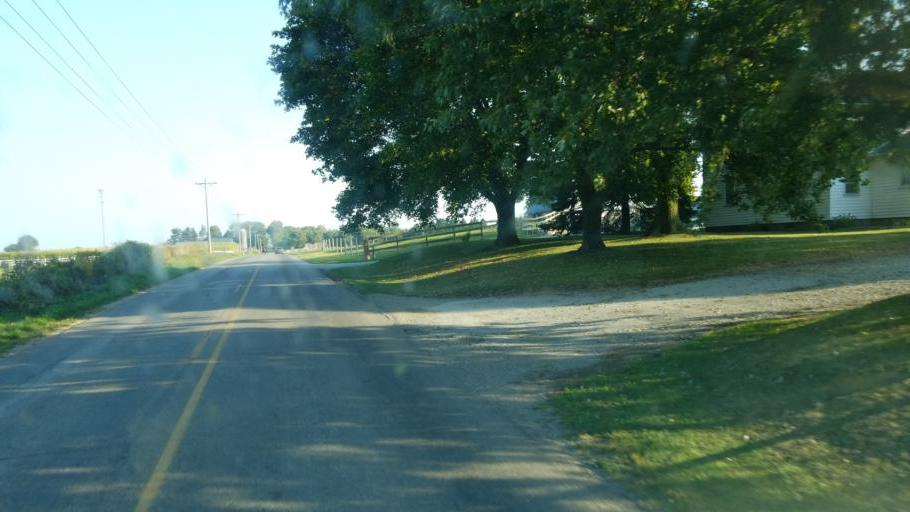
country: US
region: Indiana
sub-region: LaGrange County
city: Lagrange
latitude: 41.6165
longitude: -85.4244
